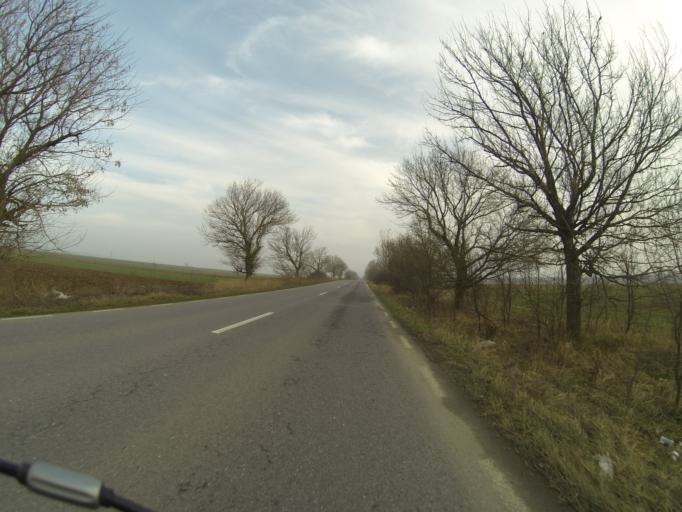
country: RO
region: Mehedinti
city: Vanju-Mare
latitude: 44.4073
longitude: 22.8914
